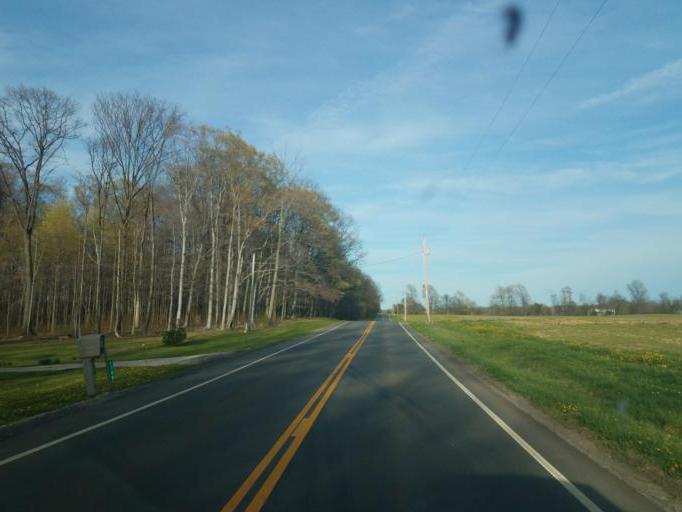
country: US
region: Ohio
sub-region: Crawford County
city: Galion
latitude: 40.6963
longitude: -82.7131
